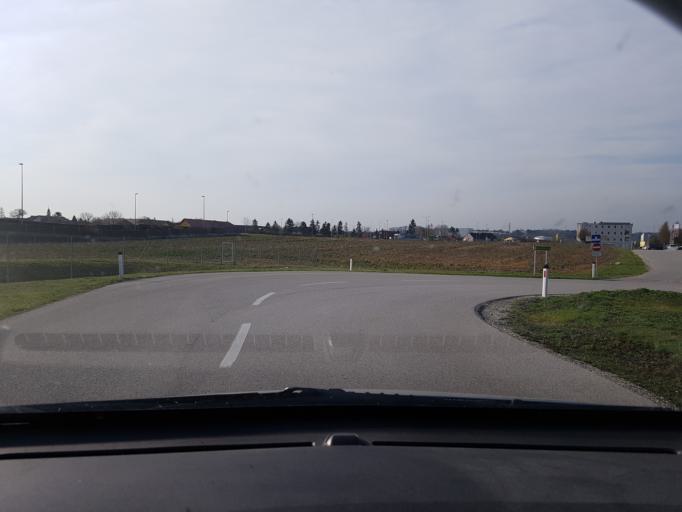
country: AT
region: Upper Austria
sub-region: Politischer Bezirk Linz-Land
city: Asten
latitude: 48.2238
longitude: 14.4117
